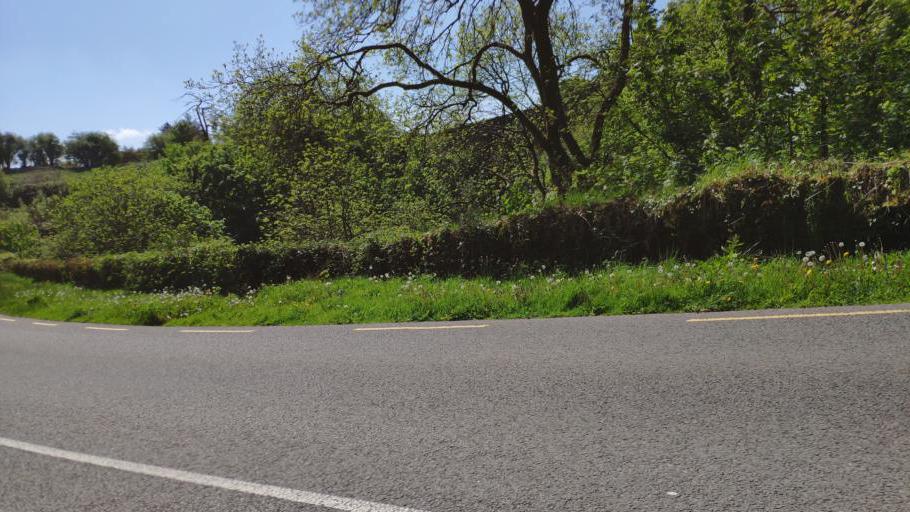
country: IE
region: Munster
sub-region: County Cork
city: Cork
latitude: 51.9274
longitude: -8.4869
